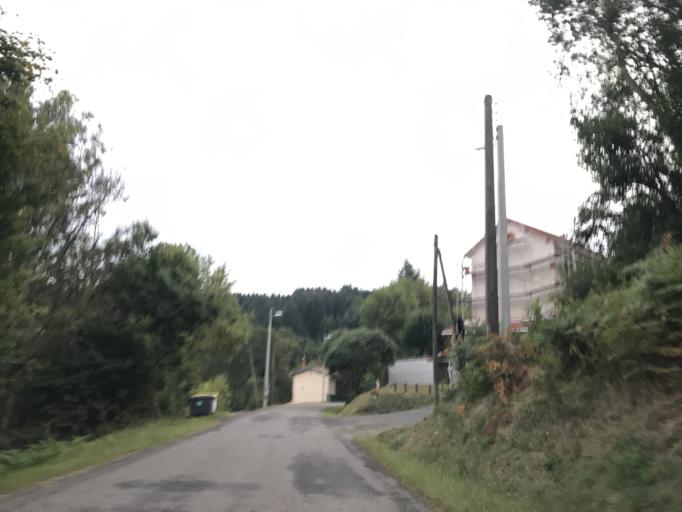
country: FR
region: Auvergne
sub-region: Departement du Puy-de-Dome
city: Thiers
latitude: 45.8499
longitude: 3.5831
